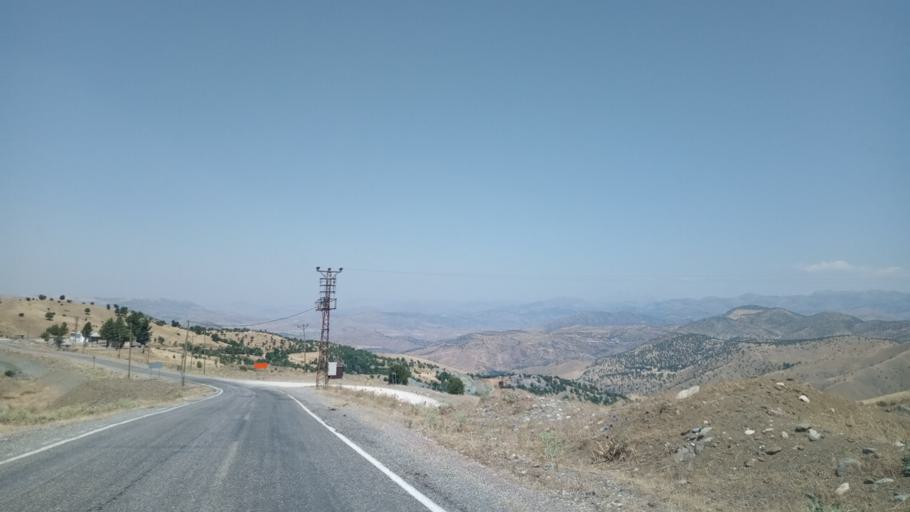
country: TR
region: Siirt
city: Dilektepe
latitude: 38.0764
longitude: 41.8262
